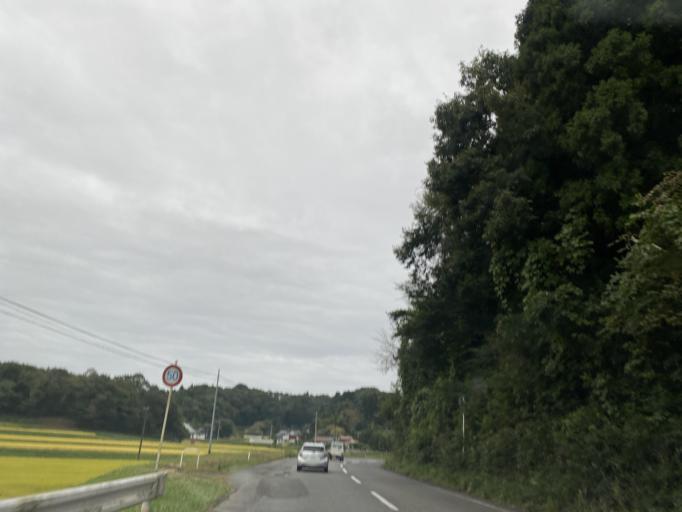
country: JP
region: Fukushima
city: Sukagawa
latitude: 37.3070
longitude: 140.2624
